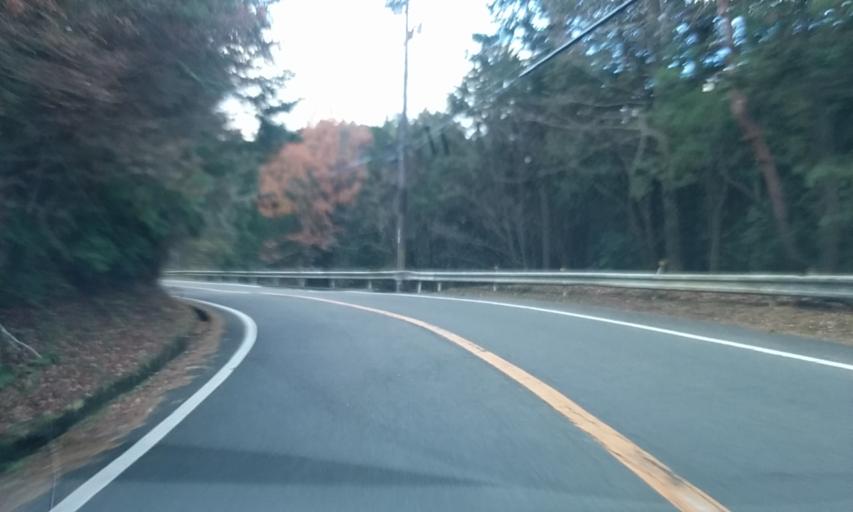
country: JP
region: Kyoto
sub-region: Kyoto-shi
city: Kamigyo-ku
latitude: 35.1108
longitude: 135.8127
